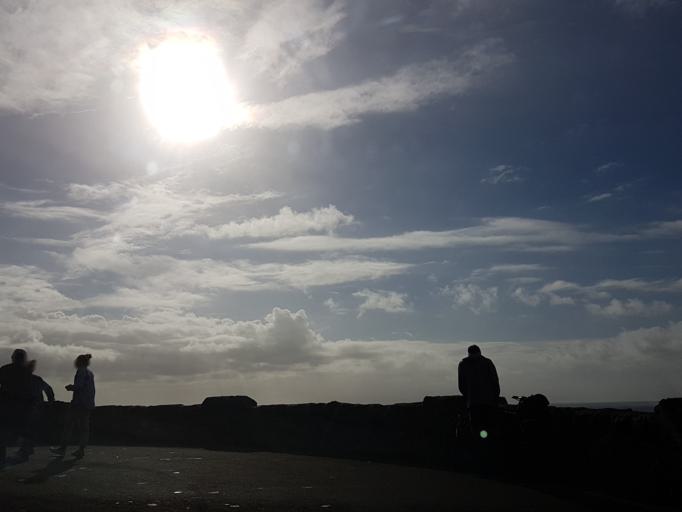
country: US
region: Oregon
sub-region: Lane County
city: Florence
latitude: 44.1257
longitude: -124.1257
